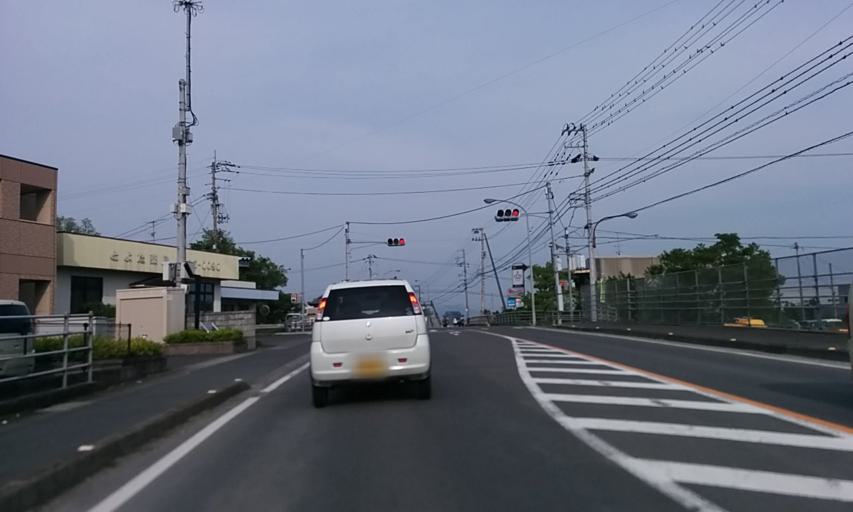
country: JP
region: Ehime
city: Kawanoecho
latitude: 33.9674
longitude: 133.4835
